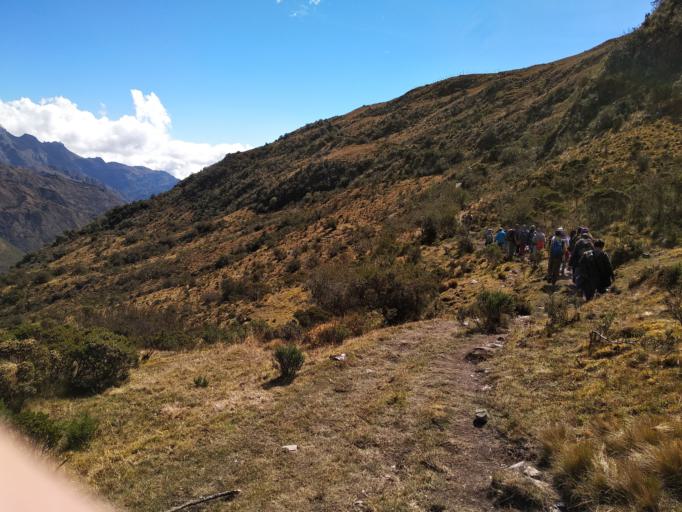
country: PE
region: Cusco
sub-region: Provincia de Urubamba
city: Ollantaytambo
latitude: -13.1281
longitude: -72.3339
